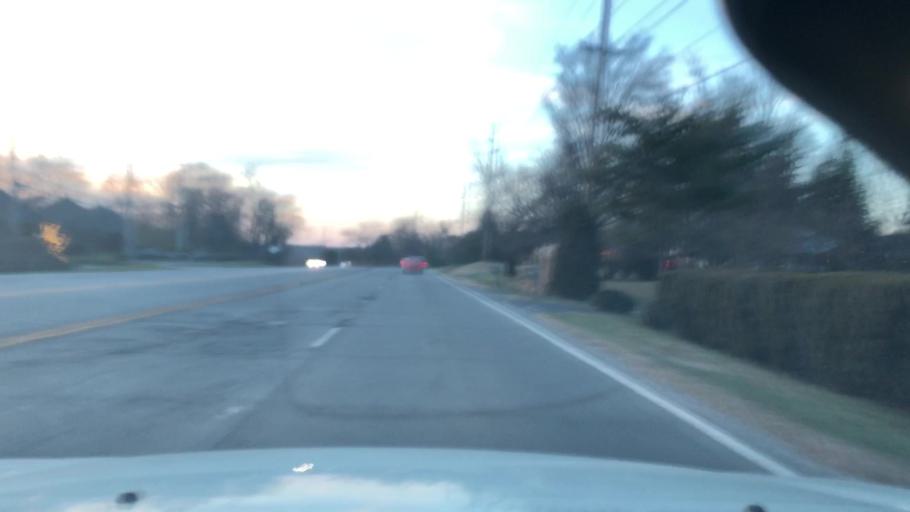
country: US
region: Kentucky
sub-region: Jefferson County
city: Anchorage
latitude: 38.2357
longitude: -85.4603
